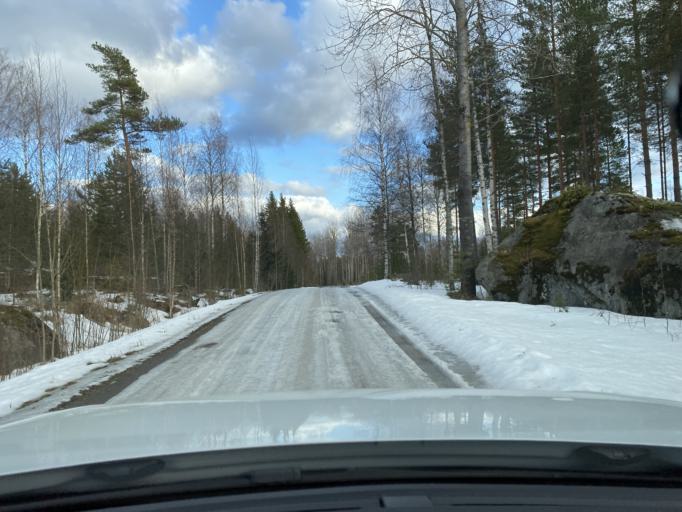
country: FI
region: Pirkanmaa
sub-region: Lounais-Pirkanmaa
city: Mouhijaervi
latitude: 61.4302
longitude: 22.9930
